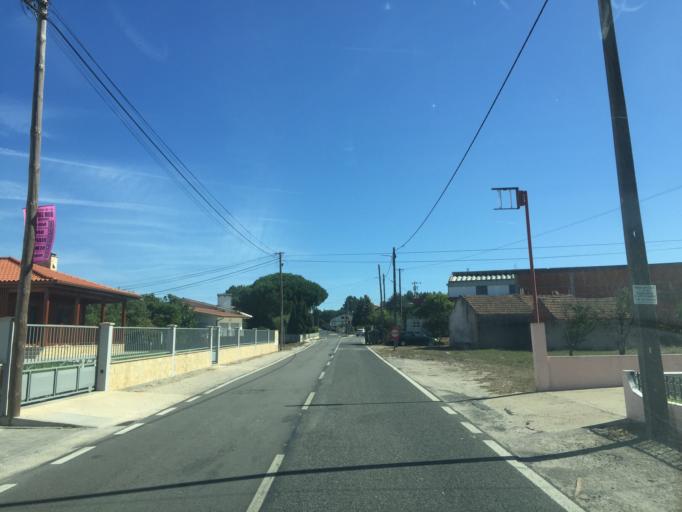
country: PT
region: Coimbra
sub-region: Figueira da Foz
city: Alhadas
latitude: 40.2181
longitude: -8.8130
